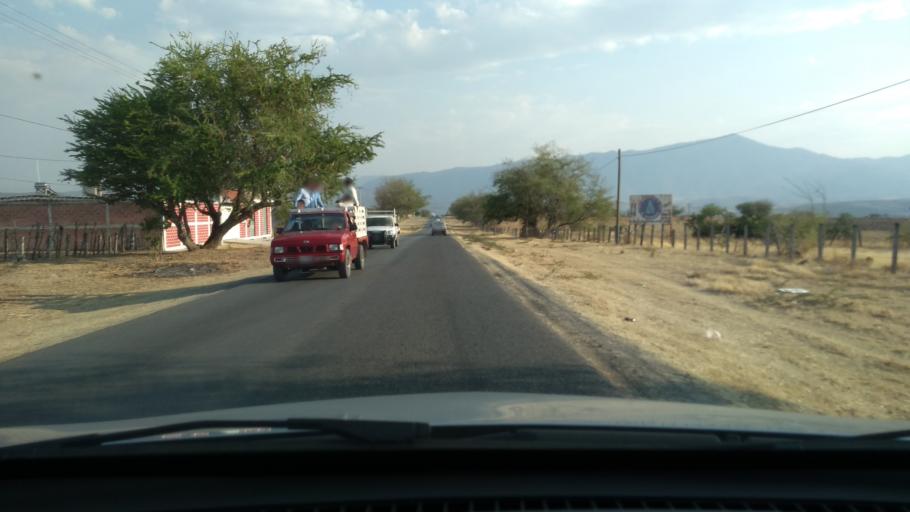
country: MX
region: Morelos
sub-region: Jojutla
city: Tehuixtla
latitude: 18.5824
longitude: -99.2641
